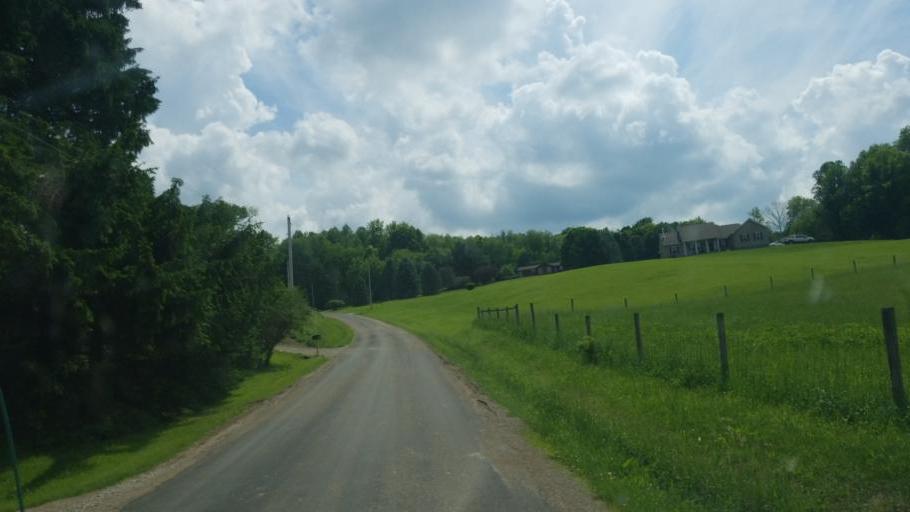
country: US
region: Ohio
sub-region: Sandusky County
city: Bellville
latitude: 40.6625
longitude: -82.4282
